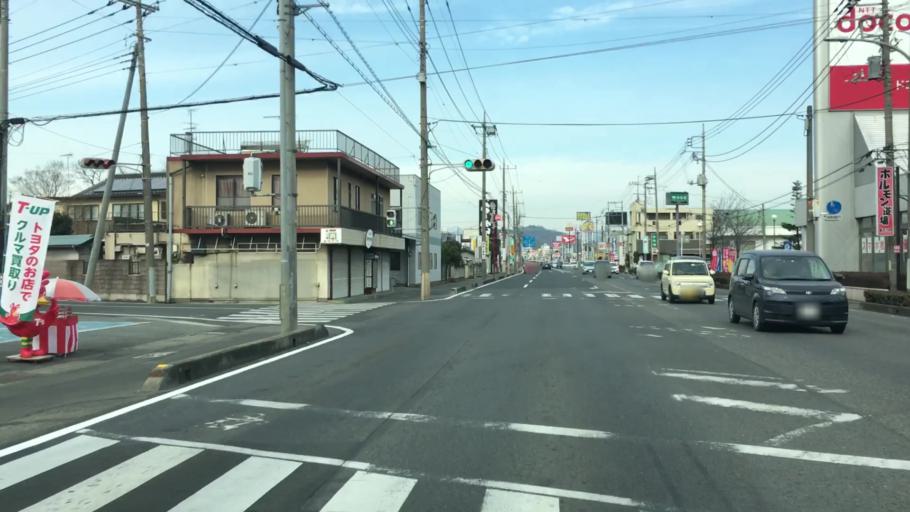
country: JP
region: Gunma
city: Ota
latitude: 36.2719
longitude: 139.3772
